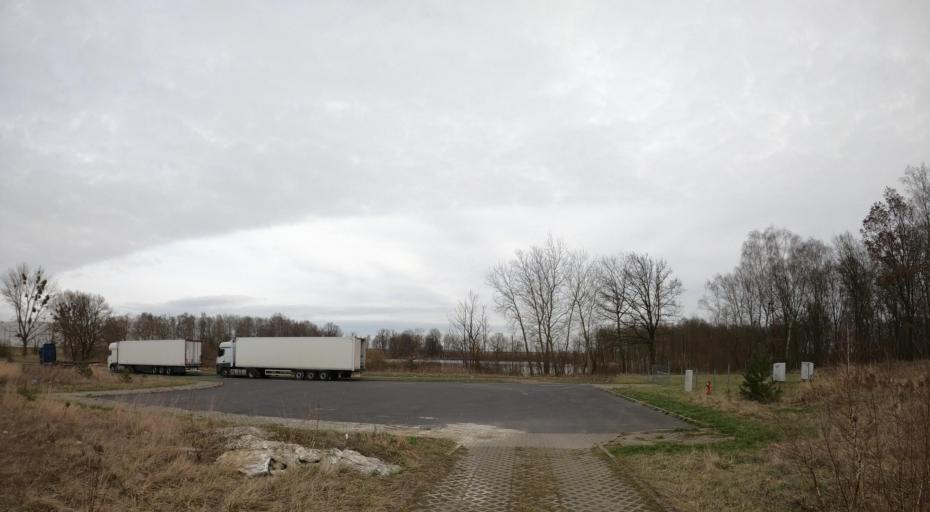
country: PL
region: West Pomeranian Voivodeship
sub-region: Powiat pyrzycki
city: Bielice
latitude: 53.2570
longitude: 14.6388
